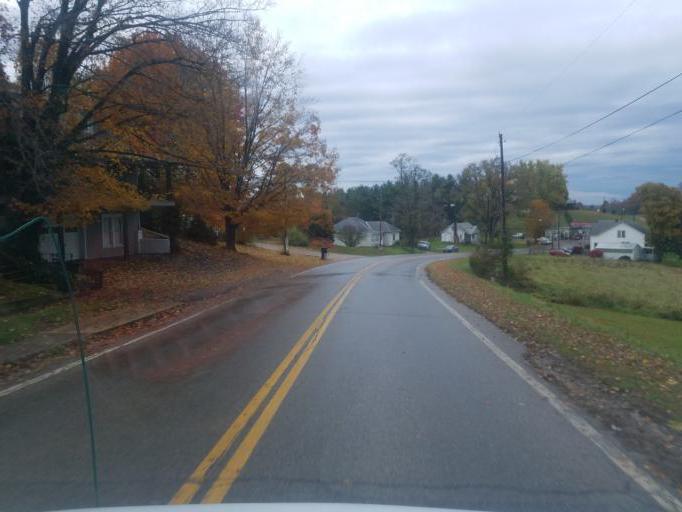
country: US
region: Ohio
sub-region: Morgan County
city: McConnelsville
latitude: 39.4949
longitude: -81.8658
